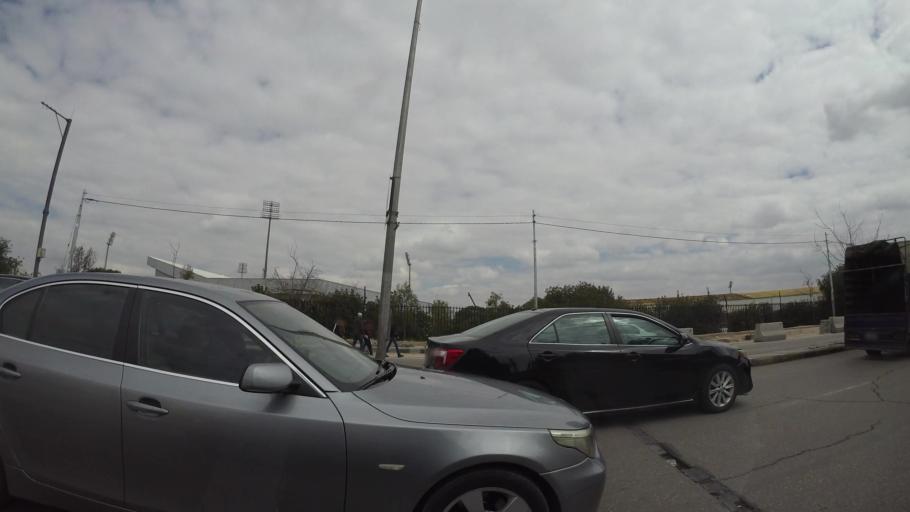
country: JO
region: Amman
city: Amman
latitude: 31.9829
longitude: 35.9010
